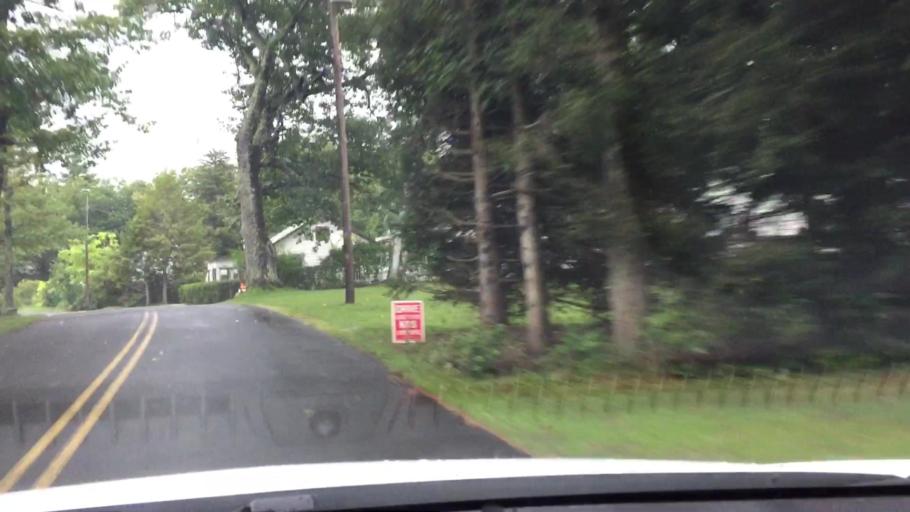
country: US
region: Massachusetts
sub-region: Berkshire County
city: Otis
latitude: 42.1527
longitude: -73.0578
